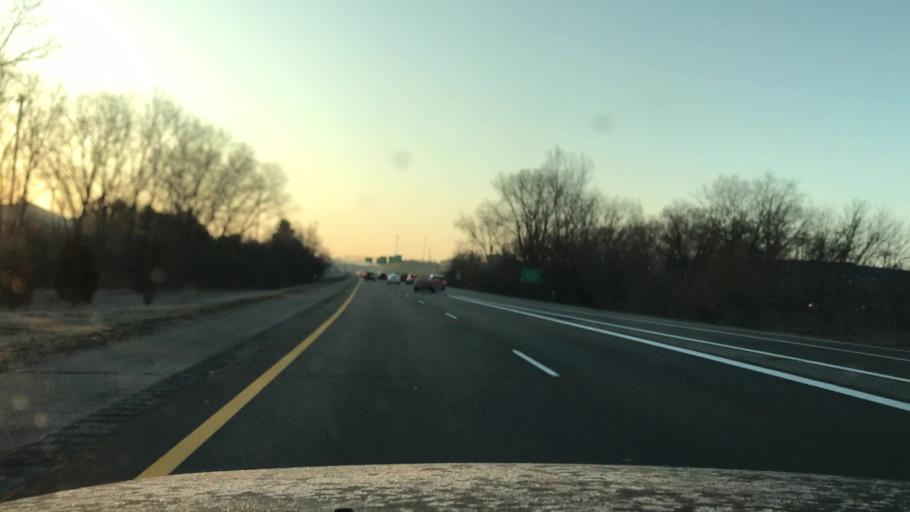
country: US
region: Michigan
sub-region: Kent County
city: East Grand Rapids
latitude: 42.9751
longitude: -85.6006
